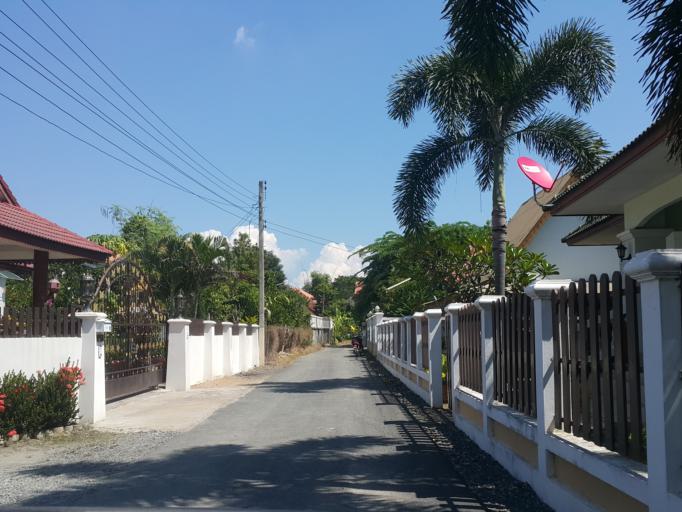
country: TH
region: Chiang Mai
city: Saraphi
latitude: 18.7623
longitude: 99.0483
